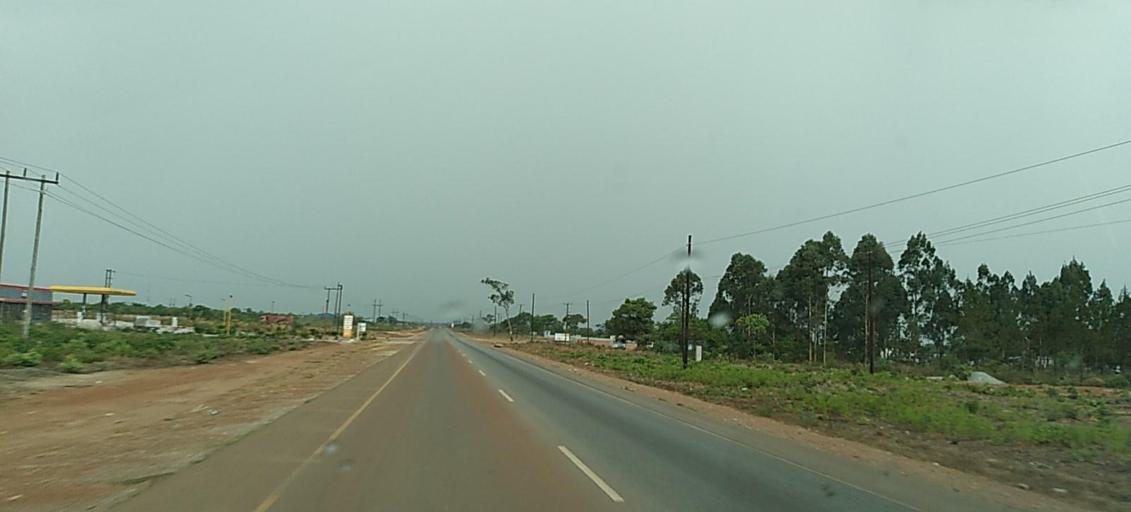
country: ZM
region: Copperbelt
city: Kalulushi
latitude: -12.8345
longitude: 28.1171
